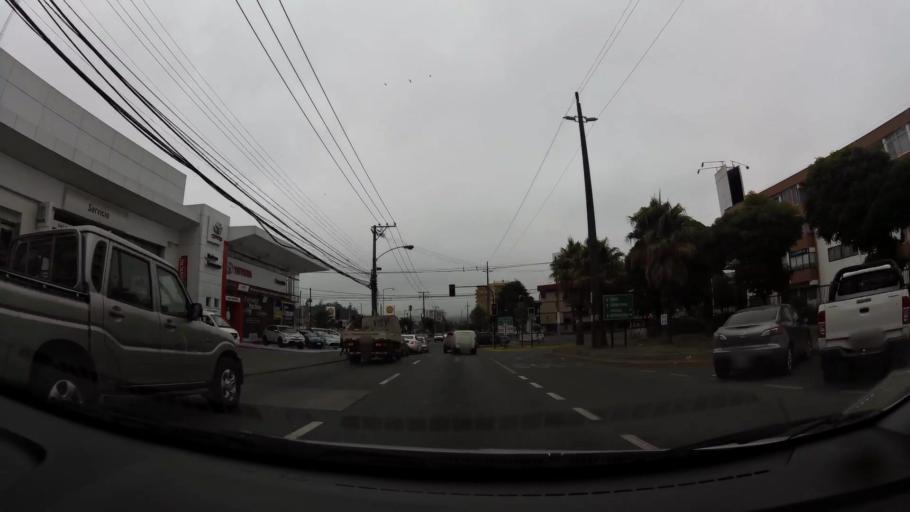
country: CL
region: Biobio
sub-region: Provincia de Concepcion
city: Concepcion
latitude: -36.8173
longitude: -73.0468
